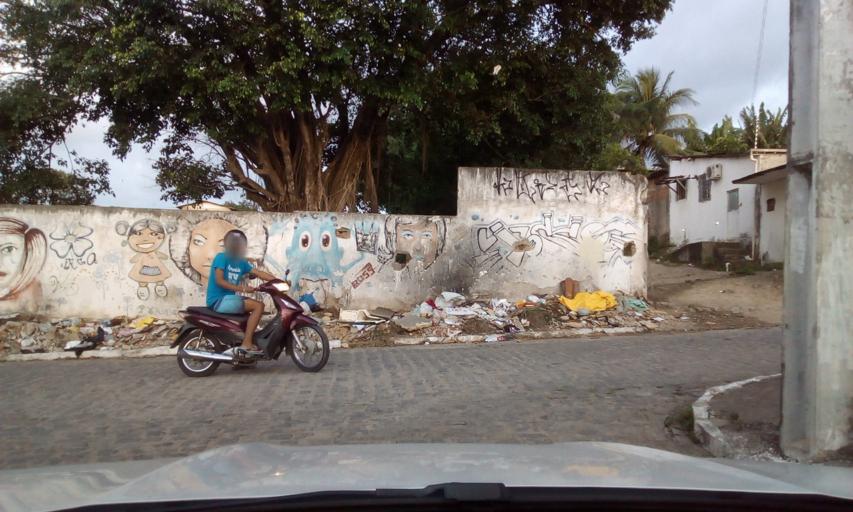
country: BR
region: Paraiba
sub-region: Joao Pessoa
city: Joao Pessoa
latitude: -7.1778
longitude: -34.8830
